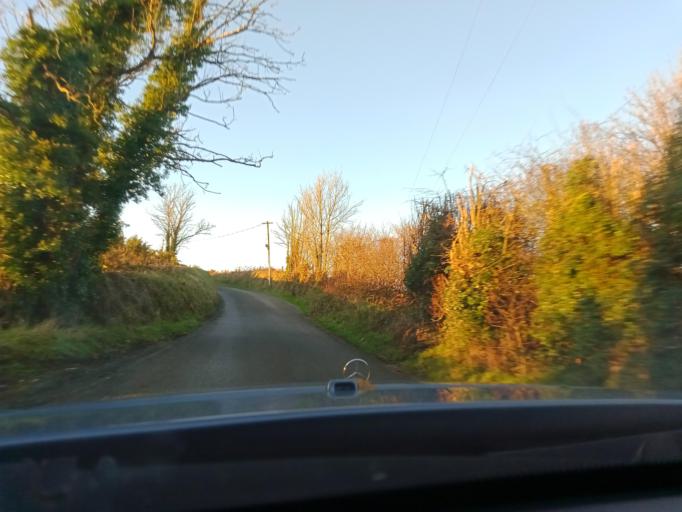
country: IE
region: Munster
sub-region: Waterford
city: Waterford
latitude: 52.3698
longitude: -7.1235
